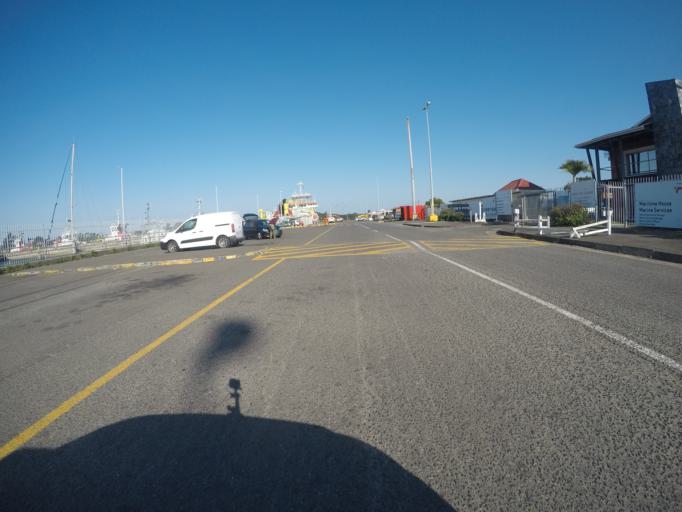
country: ZA
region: KwaZulu-Natal
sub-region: uThungulu District Municipality
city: Richards Bay
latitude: -28.7947
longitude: 32.0780
